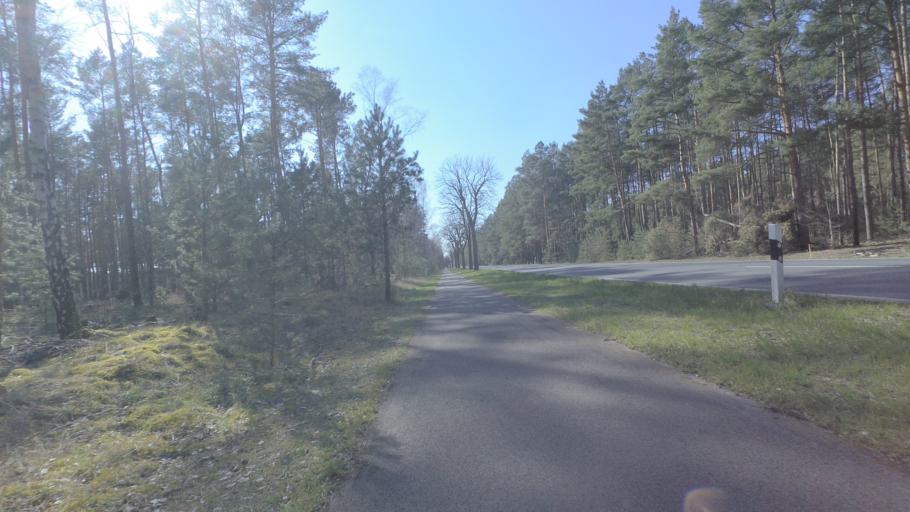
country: DE
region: Brandenburg
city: Halbe
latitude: 52.1072
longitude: 13.7278
